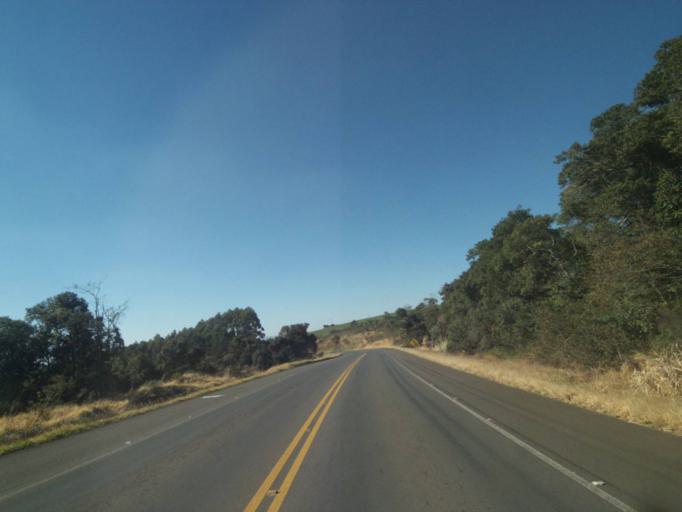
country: BR
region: Parana
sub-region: Tibagi
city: Tibagi
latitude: -24.7548
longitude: -50.4683
